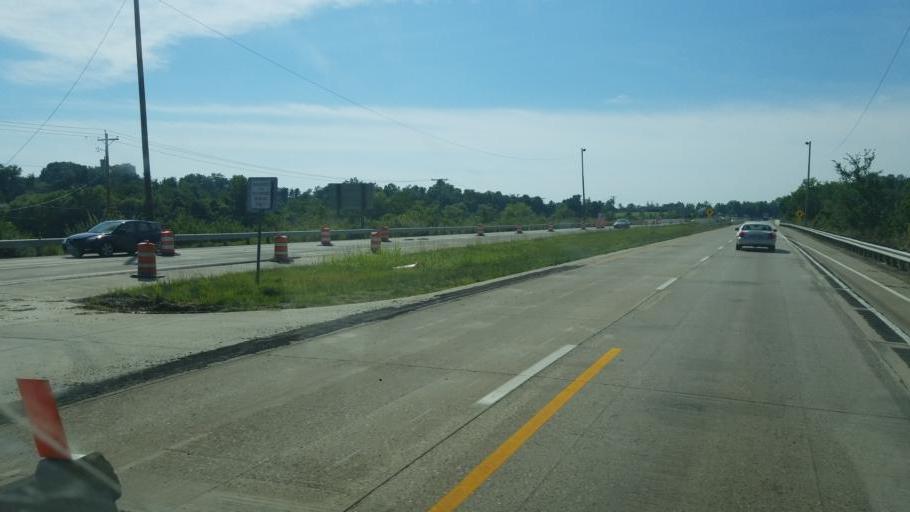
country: US
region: Ohio
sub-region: Athens County
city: The Plains
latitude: 39.3651
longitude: -82.1141
